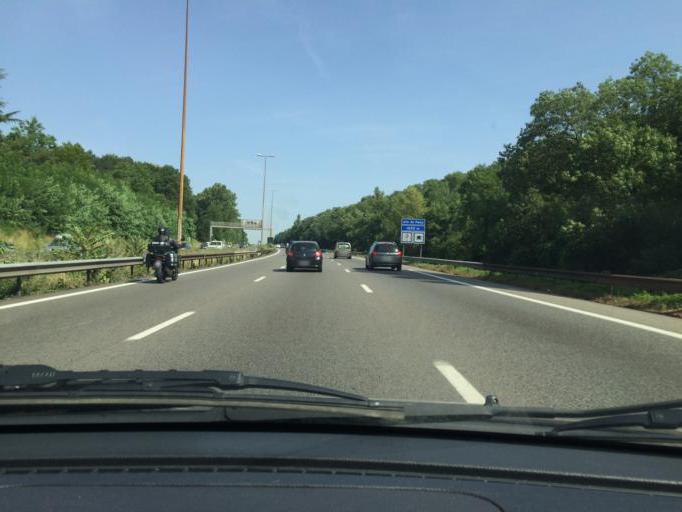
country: FR
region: Rhone-Alpes
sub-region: Departement du Rhone
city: Ecully
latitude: 45.7924
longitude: 4.7821
